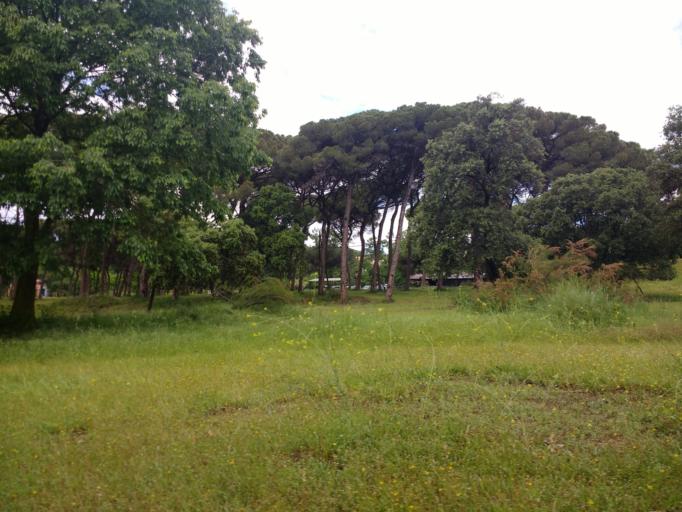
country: ES
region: Catalonia
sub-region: Provincia de Barcelona
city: Polinya
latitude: 41.5666
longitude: 2.1761
